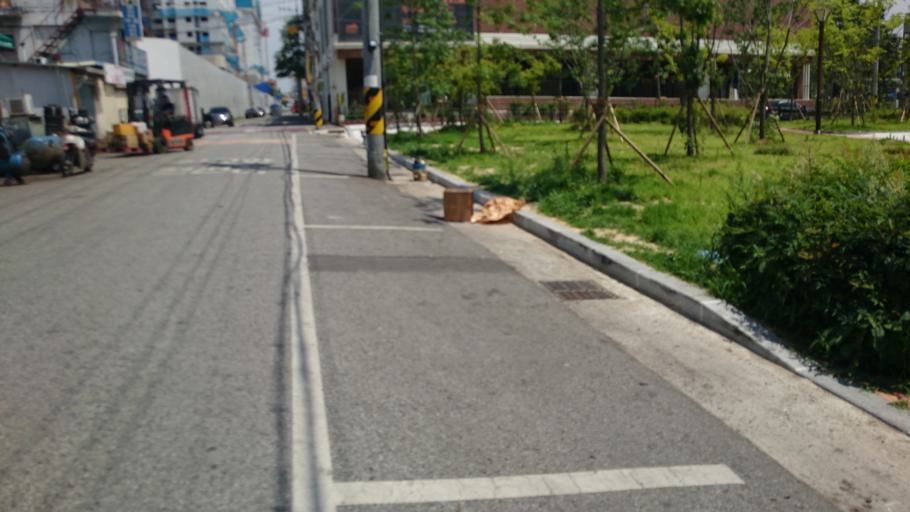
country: KR
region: Daegu
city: Daegu
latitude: 35.8760
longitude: 128.5836
